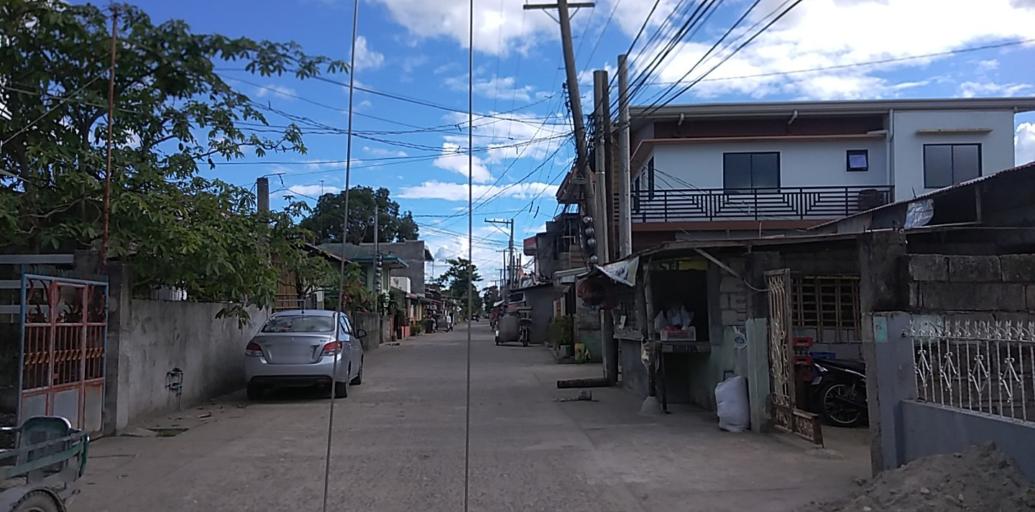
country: PH
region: Central Luzon
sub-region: Province of Pampanga
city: Arayat
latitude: 15.1452
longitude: 120.7673
